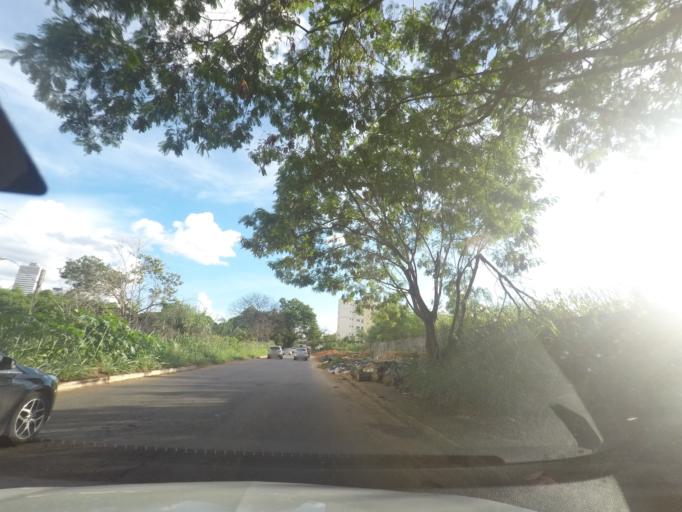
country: BR
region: Goias
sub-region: Goiania
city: Goiania
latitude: -16.6897
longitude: -49.2929
